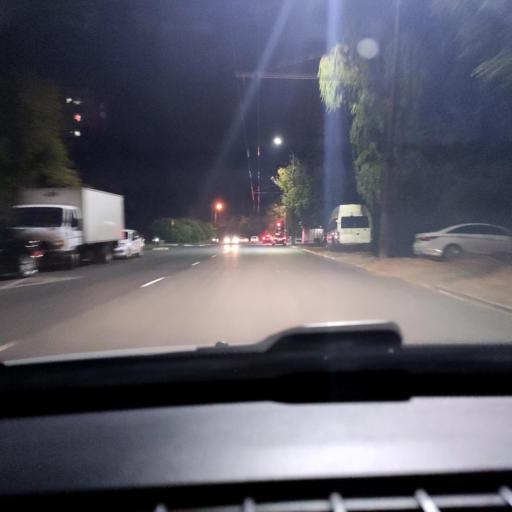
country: RU
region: Voronezj
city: Voronezh
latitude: 51.6987
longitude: 39.1940
